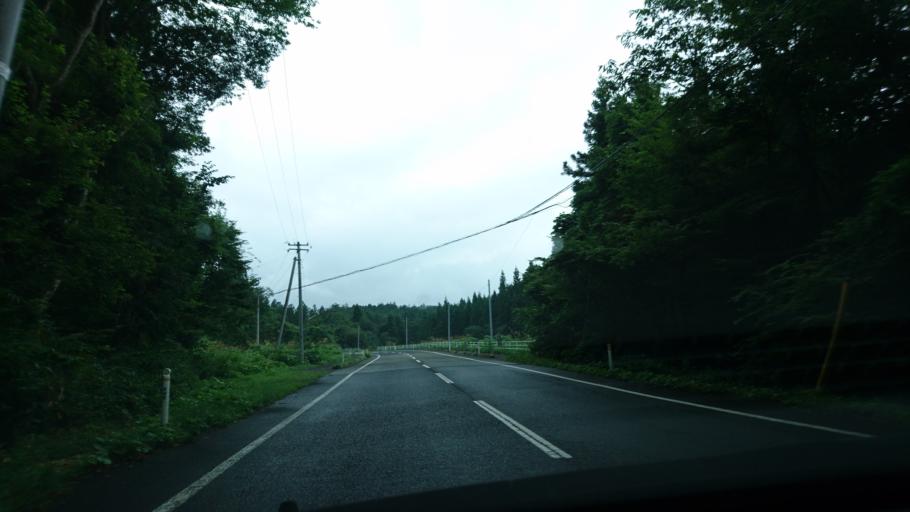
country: JP
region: Iwate
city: Ichinoseki
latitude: 38.8896
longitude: 140.9612
